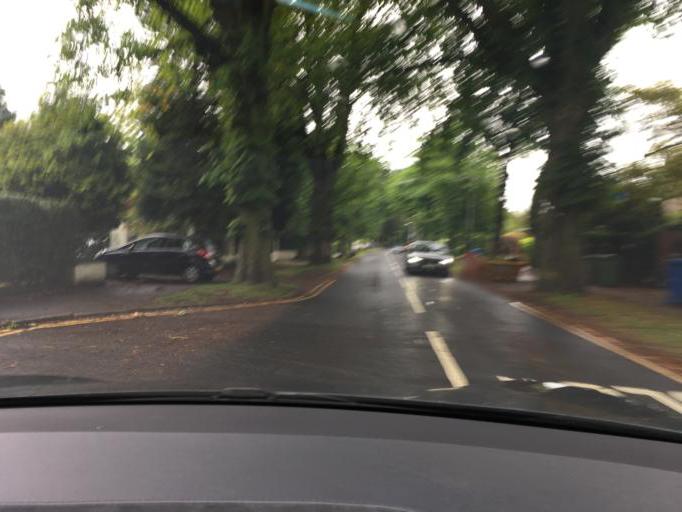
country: GB
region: England
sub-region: Borough of Stockport
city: Bramhall
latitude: 53.3769
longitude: -2.1619
